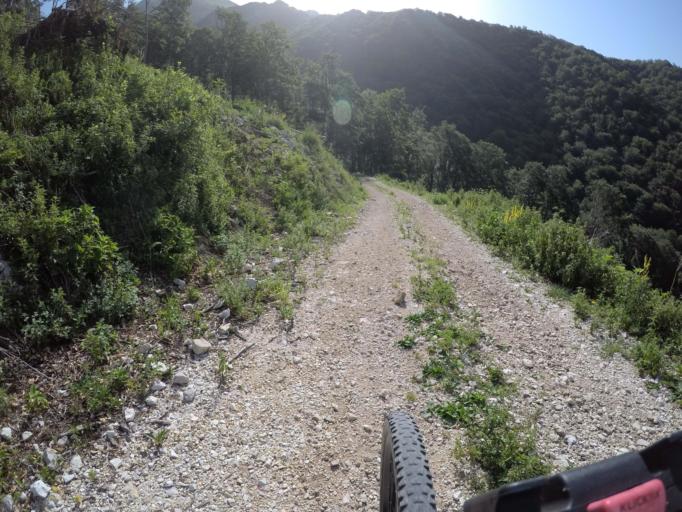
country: IT
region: Friuli Venezia Giulia
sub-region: Provincia di Udine
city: Resiutta
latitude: 46.3337
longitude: 13.2162
